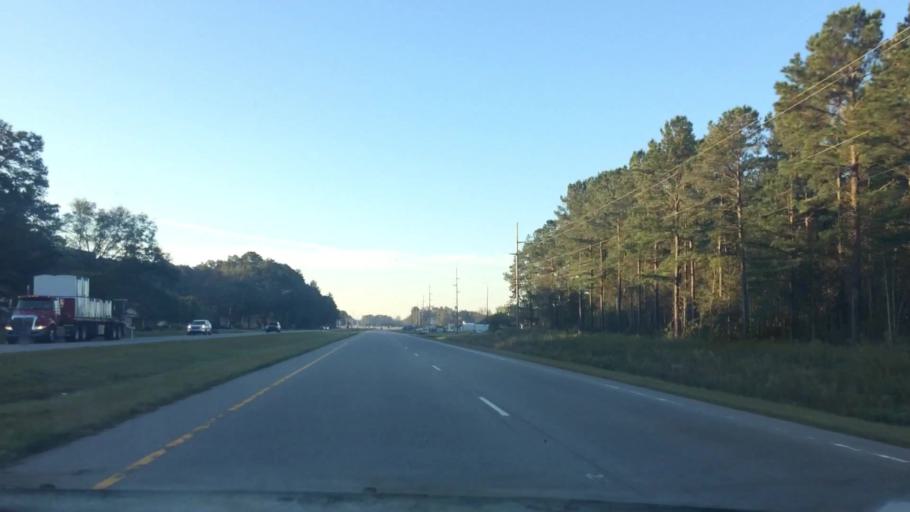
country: US
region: North Carolina
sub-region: Pitt County
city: Grifton
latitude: 35.4177
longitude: -77.4345
